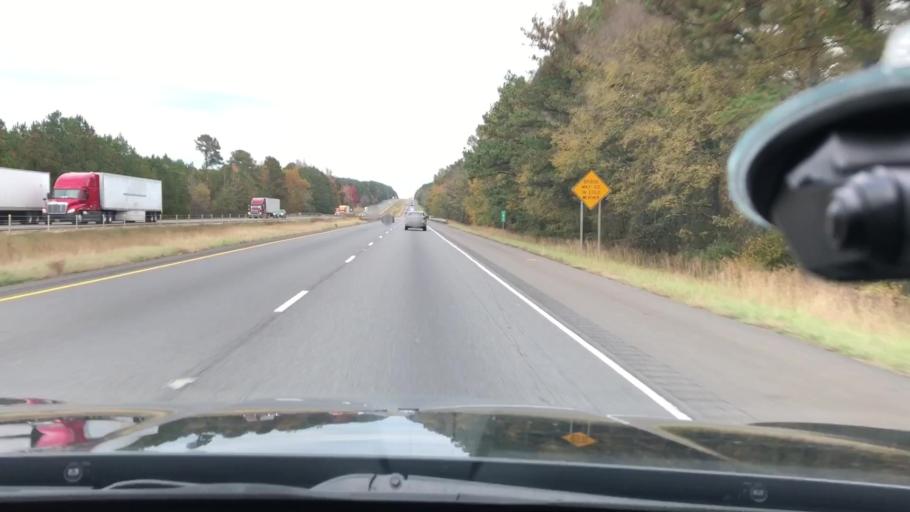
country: US
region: Arkansas
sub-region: Clark County
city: Arkadelphia
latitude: 34.2609
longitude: -92.9809
